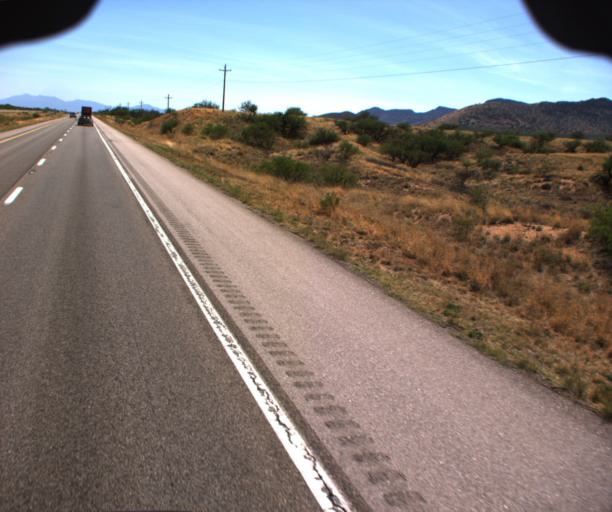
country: US
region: Arizona
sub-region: Cochise County
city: Whetstone
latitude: 31.8735
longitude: -110.3413
